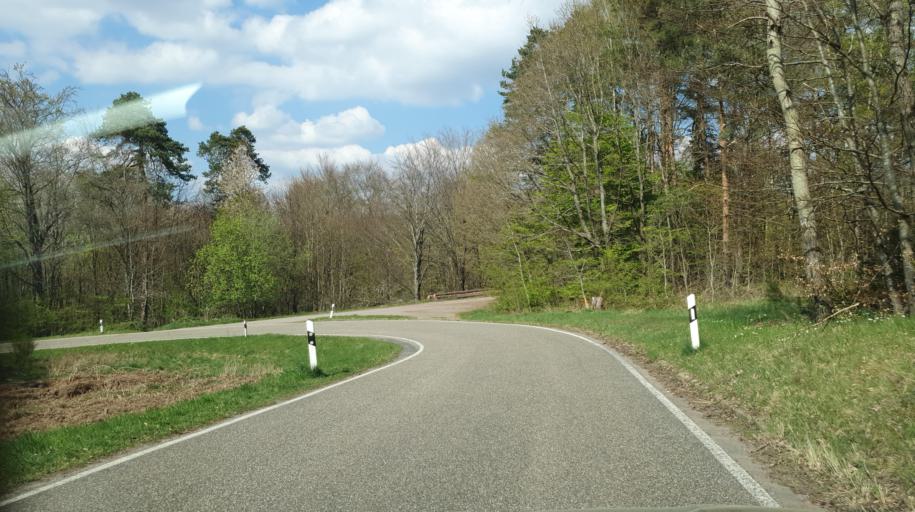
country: DE
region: Rheinland-Pfalz
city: Leimen
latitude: 49.2753
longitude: 7.7642
